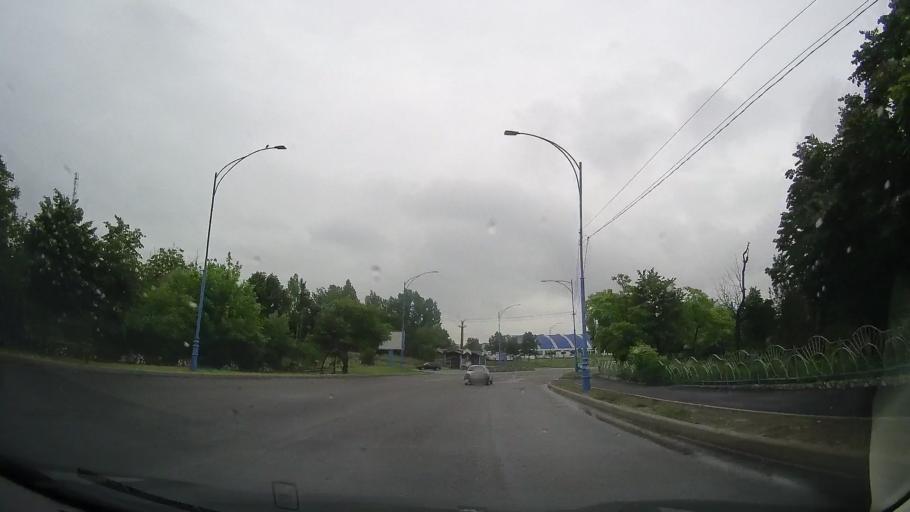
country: RO
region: Mehedinti
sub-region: Municipiul Drobeta-Turnu Severin
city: Drobeta-Turnu Severin
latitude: 44.6283
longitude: 22.6385
